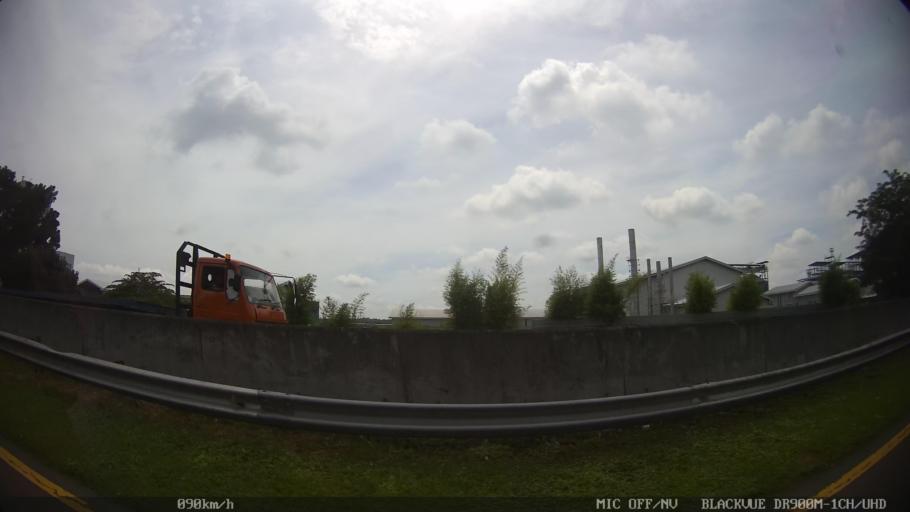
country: ID
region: North Sumatra
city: Labuhan Deli
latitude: 3.6827
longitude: 98.6809
